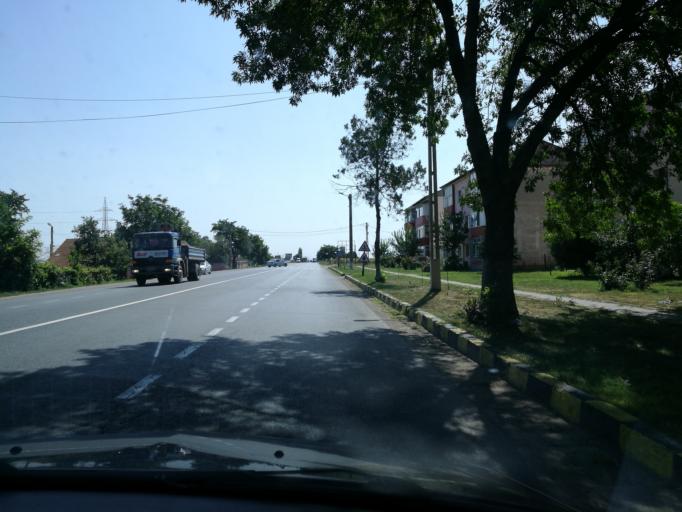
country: RO
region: Bacau
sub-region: Comuna Sascut
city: Sascut
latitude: 46.2046
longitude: 27.1104
